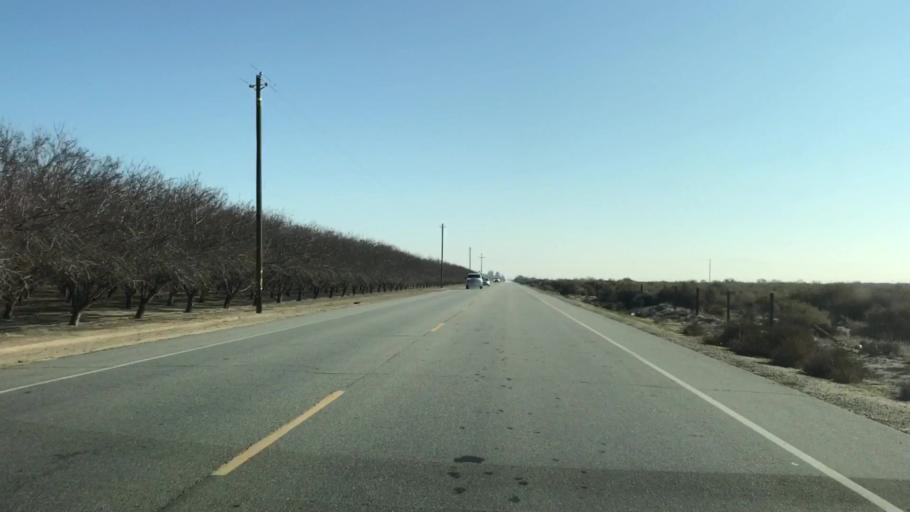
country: US
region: California
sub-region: Kern County
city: Shafter
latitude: 35.3546
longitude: -119.3097
